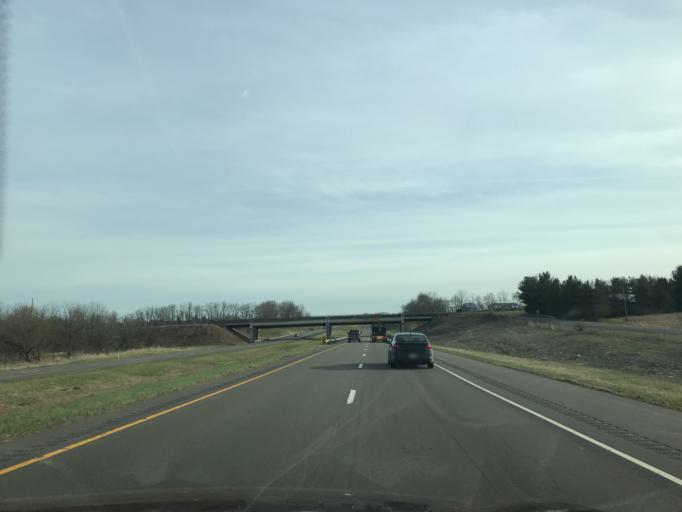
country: US
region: Pennsylvania
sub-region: Northumberland County
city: Watsontown
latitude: 41.1011
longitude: -76.8094
